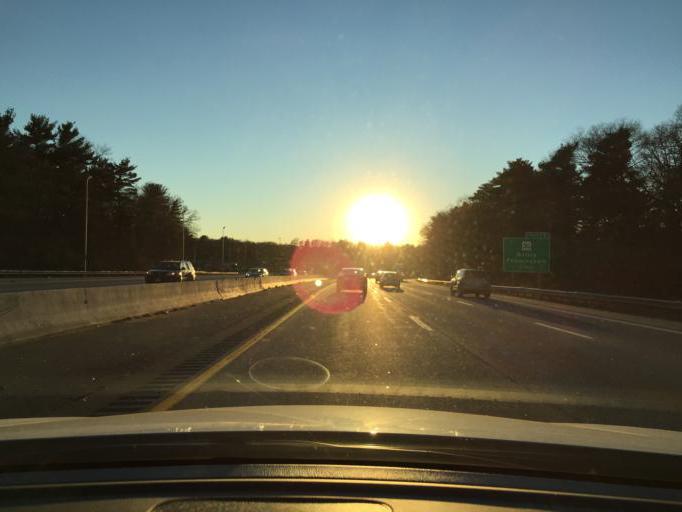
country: US
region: Massachusetts
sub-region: Middlesex County
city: Cochituate
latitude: 42.3140
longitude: -71.3616
